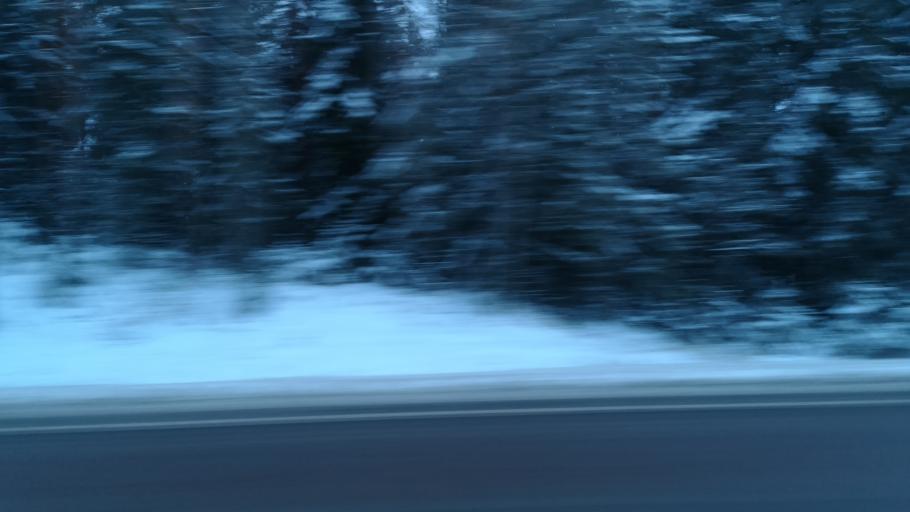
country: FI
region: Southern Savonia
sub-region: Savonlinna
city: Sulkava
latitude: 61.9443
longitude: 28.5119
